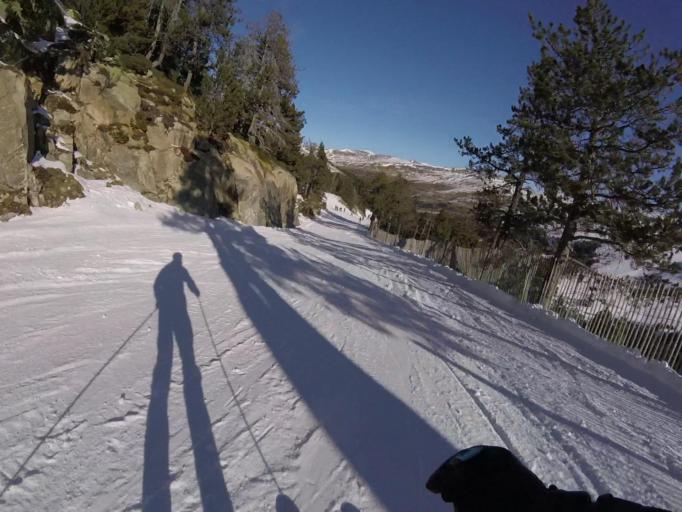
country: AD
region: Encamp
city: Pas de la Casa
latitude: 42.5269
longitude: 1.6892
